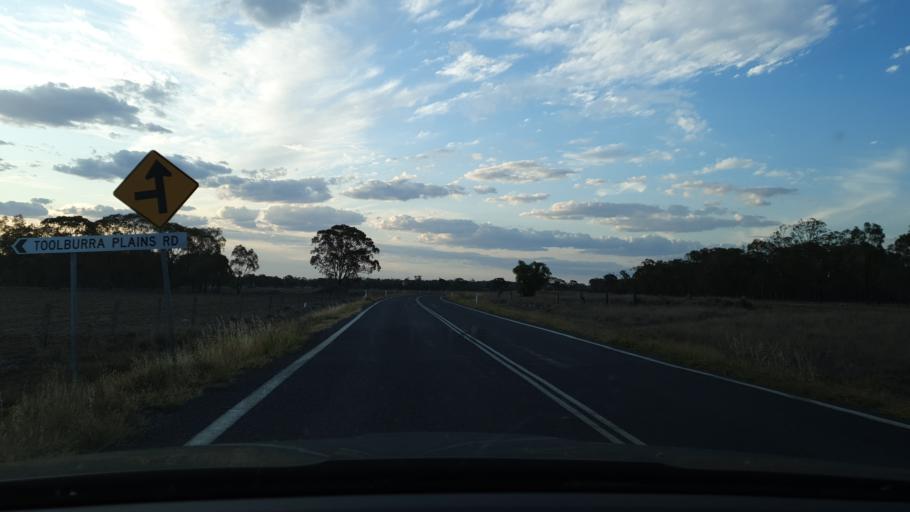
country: AU
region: Queensland
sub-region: Southern Downs
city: Warwick
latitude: -28.1636
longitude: 151.9683
